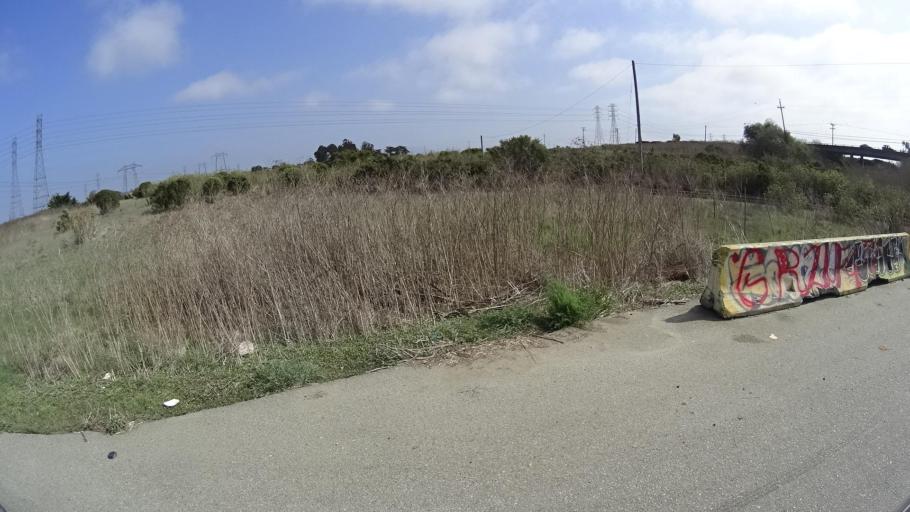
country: US
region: California
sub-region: Monterey County
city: Elkhorn
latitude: 36.7978
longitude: -121.7540
